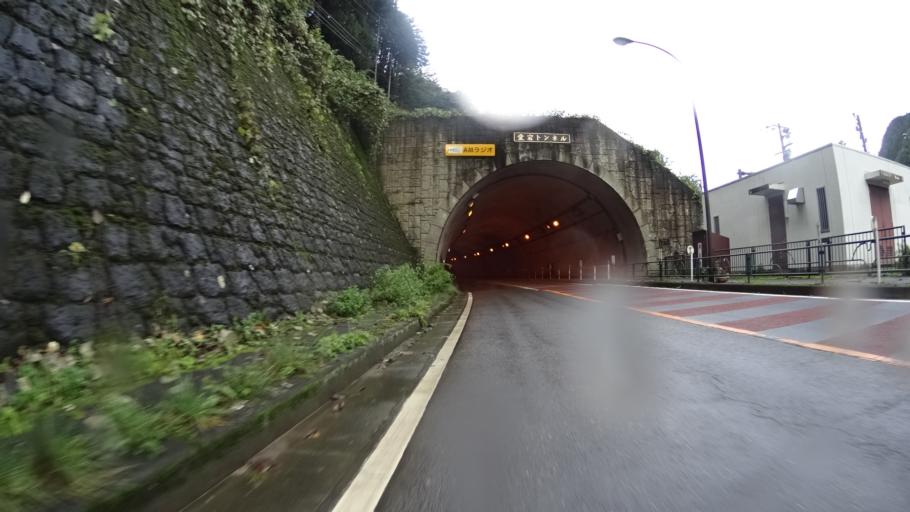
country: JP
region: Tokyo
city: Itsukaichi
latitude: 35.8020
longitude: 139.1033
